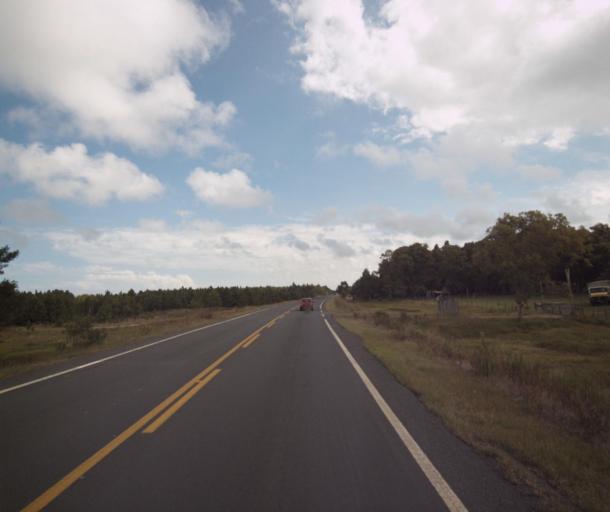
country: BR
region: Rio Grande do Sul
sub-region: Tapes
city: Tapes
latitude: -31.4112
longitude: -51.1693
